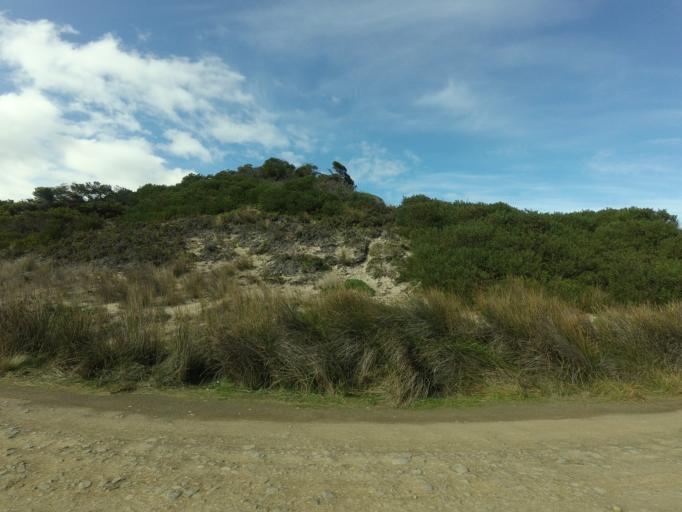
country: AU
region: Tasmania
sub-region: Clarence
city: Sandford
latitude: -43.0849
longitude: 147.6738
